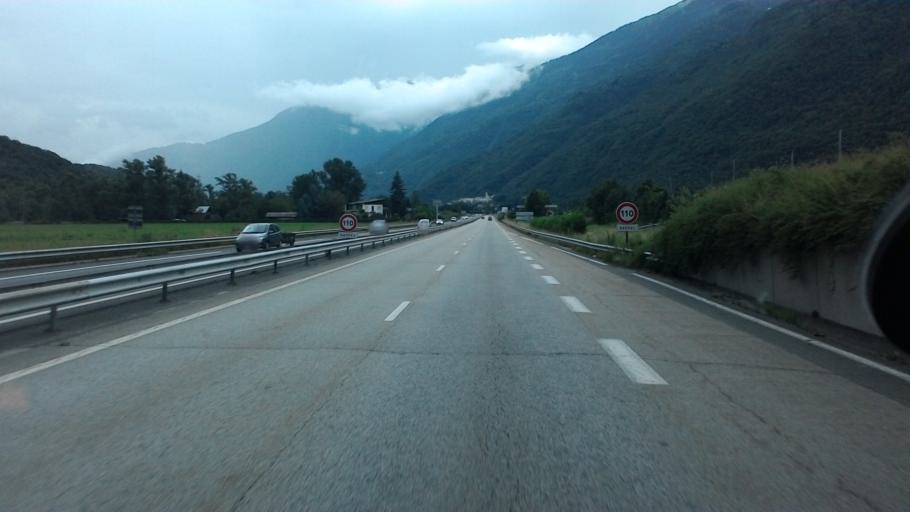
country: FR
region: Rhone-Alpes
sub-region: Departement de la Savoie
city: La Bathie
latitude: 45.5976
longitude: 6.4480
